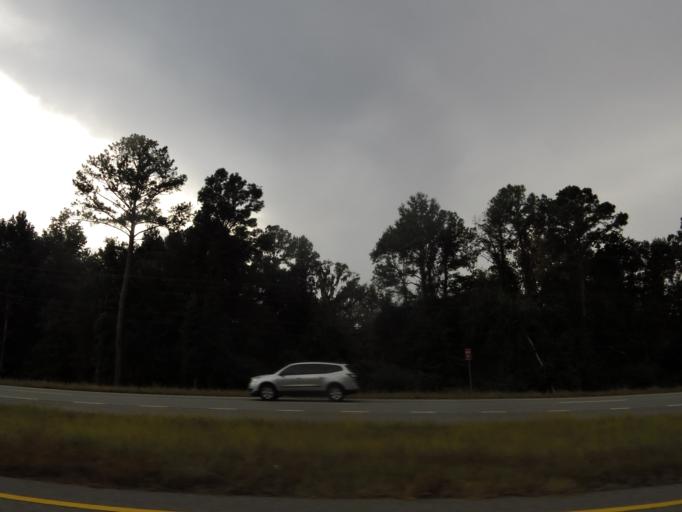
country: US
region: Georgia
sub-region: McIntosh County
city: Darien
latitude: 31.3873
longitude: -81.6395
